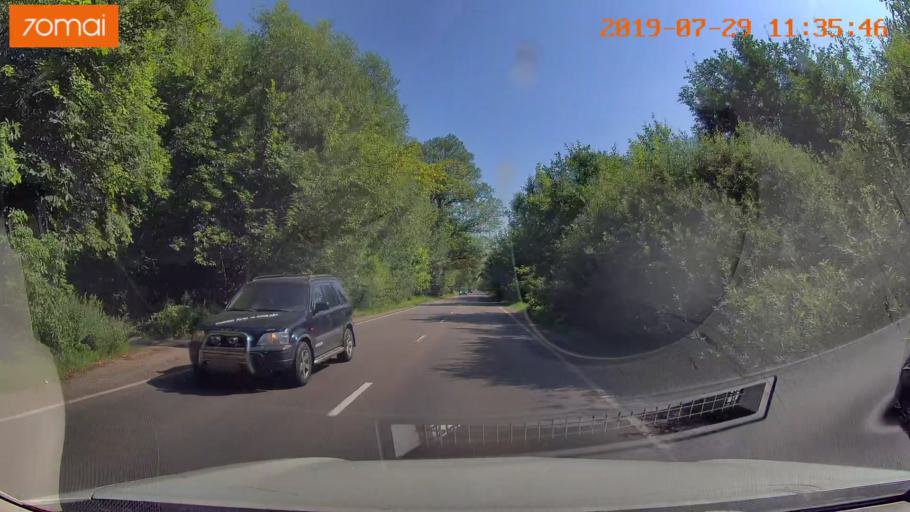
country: RU
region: Kaliningrad
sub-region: Gorod Kaliningrad
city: Kaliningrad
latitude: 54.6594
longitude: 20.5582
